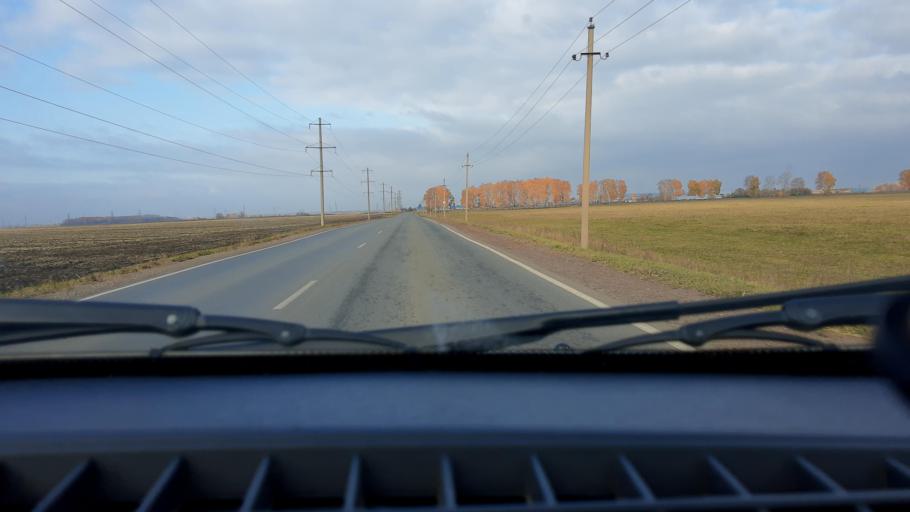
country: RU
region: Bashkortostan
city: Kabakovo
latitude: 54.5416
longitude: 56.0553
